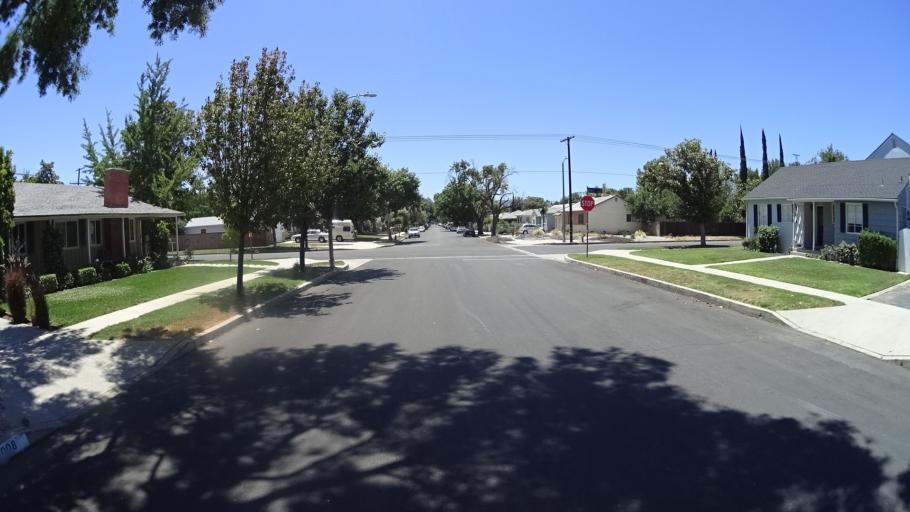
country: US
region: California
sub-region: Los Angeles County
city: Northridge
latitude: 34.1978
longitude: -118.5163
